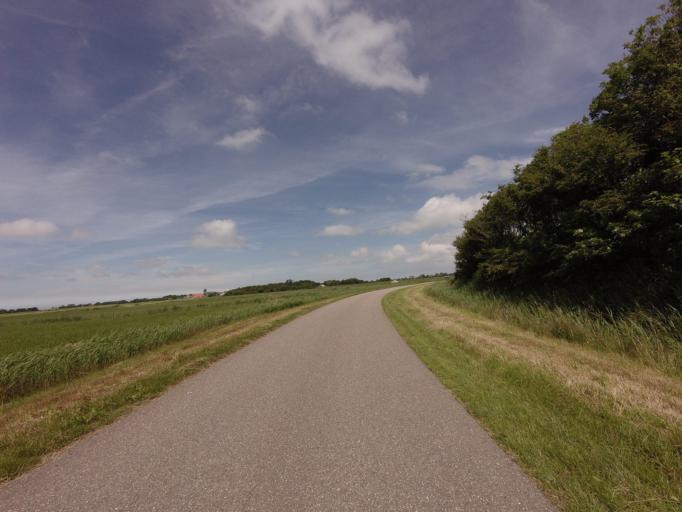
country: NL
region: North Holland
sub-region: Gemeente Texel
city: Den Burg
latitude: 53.0772
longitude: 4.8807
